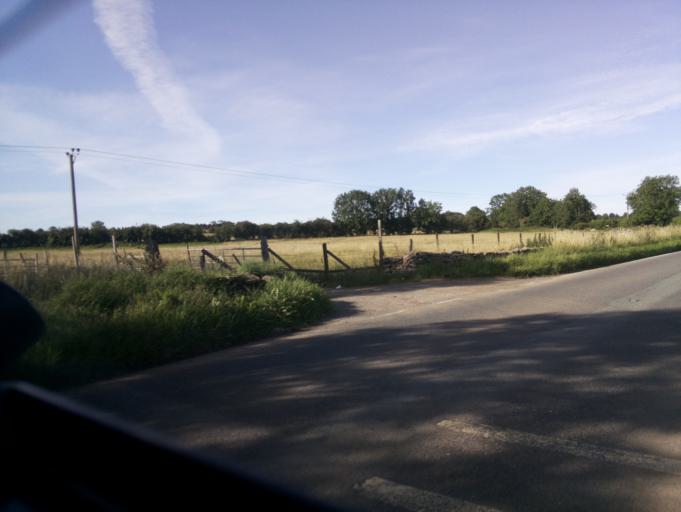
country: GB
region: England
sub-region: Bath and North East Somerset
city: Compton Dando
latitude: 51.3962
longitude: -2.5222
